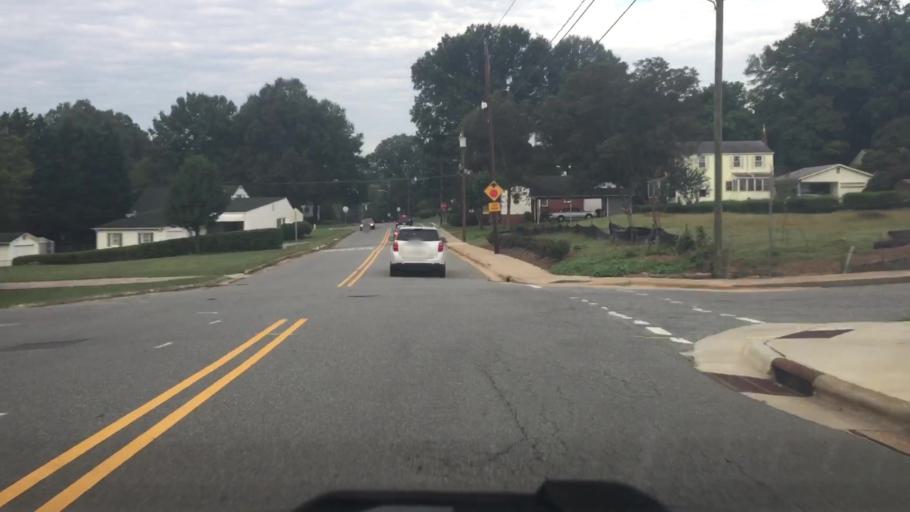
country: US
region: North Carolina
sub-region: Iredell County
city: Mooresville
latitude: 35.5760
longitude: -80.8026
